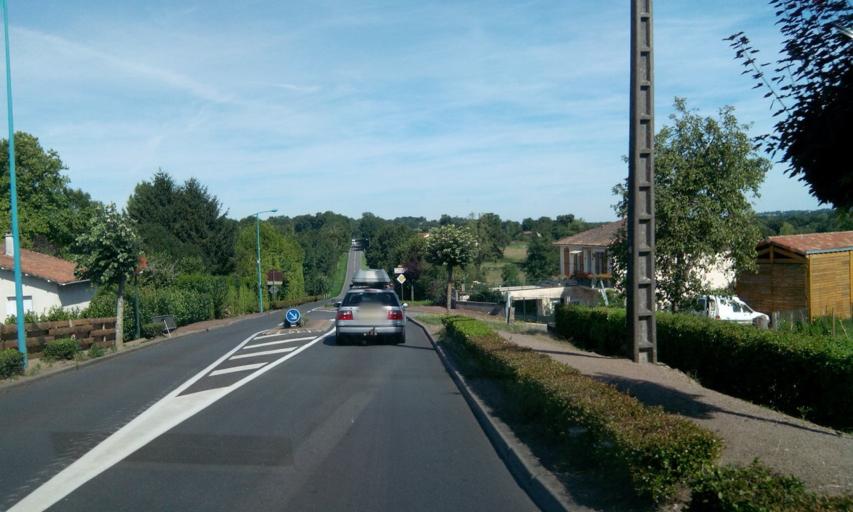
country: FR
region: Poitou-Charentes
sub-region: Departement de la Charente
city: Confolens
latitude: 45.9650
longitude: 0.6984
